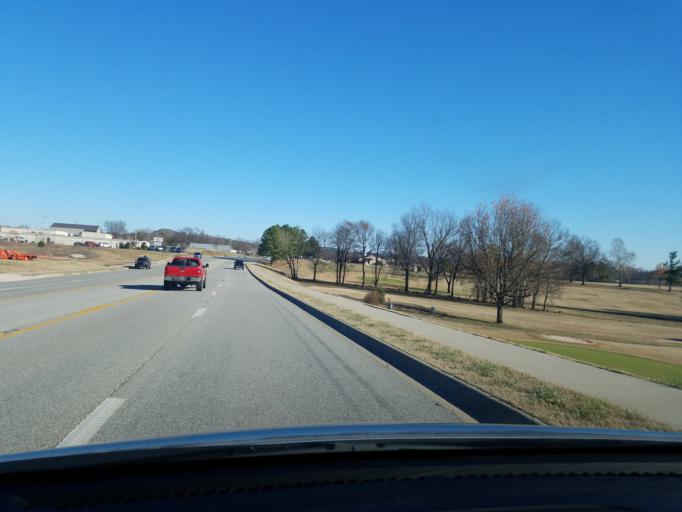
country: US
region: Arkansas
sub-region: Carroll County
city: Berryville
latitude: 36.3822
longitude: -93.5985
